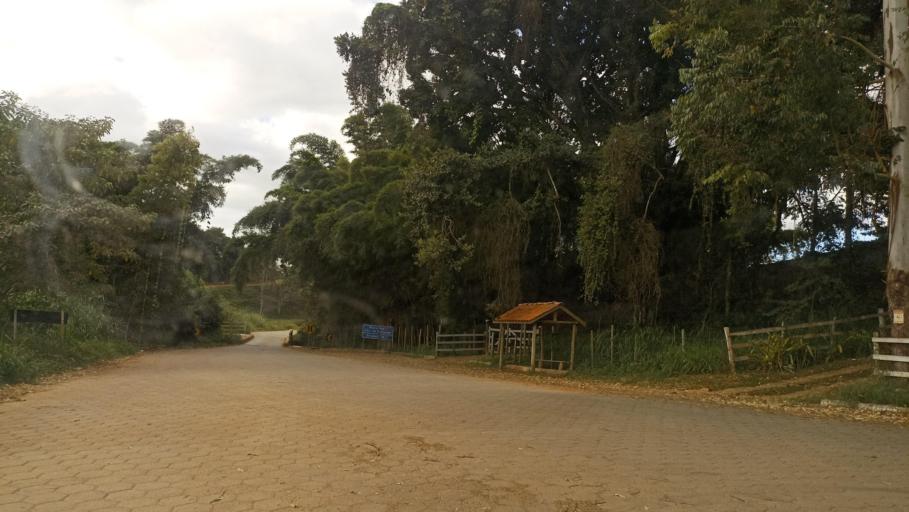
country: BR
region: Minas Gerais
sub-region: Tiradentes
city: Tiradentes
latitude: -21.0942
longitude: -44.0739
